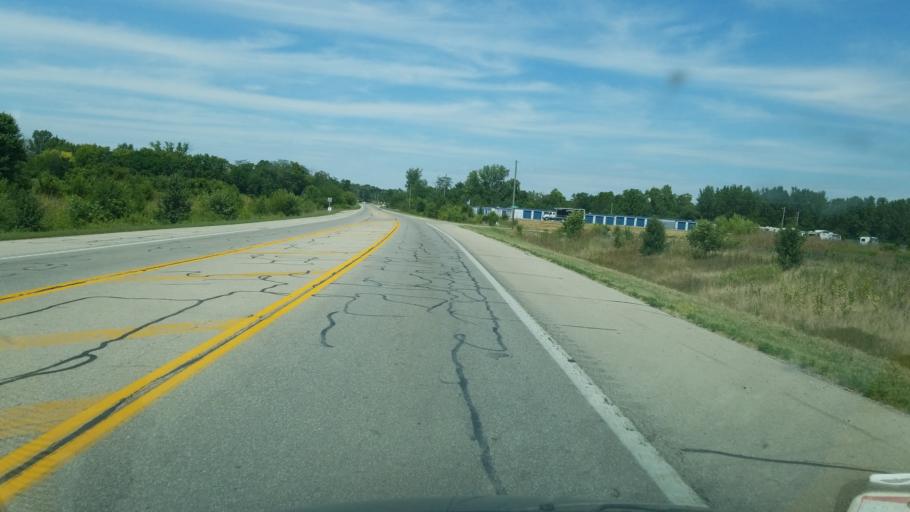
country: US
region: Ohio
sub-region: Madison County
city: Plain City
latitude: 40.1196
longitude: -83.2724
